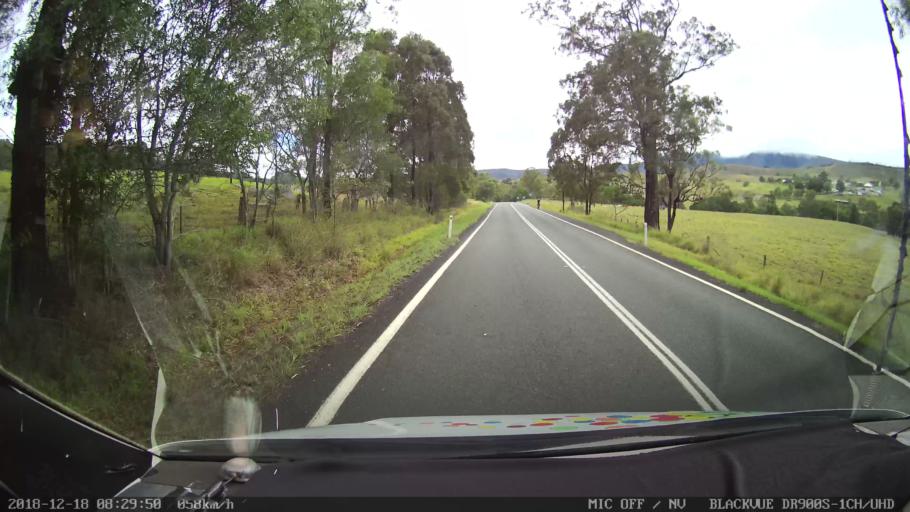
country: AU
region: New South Wales
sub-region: Kyogle
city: Kyogle
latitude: -28.3244
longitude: 152.7629
